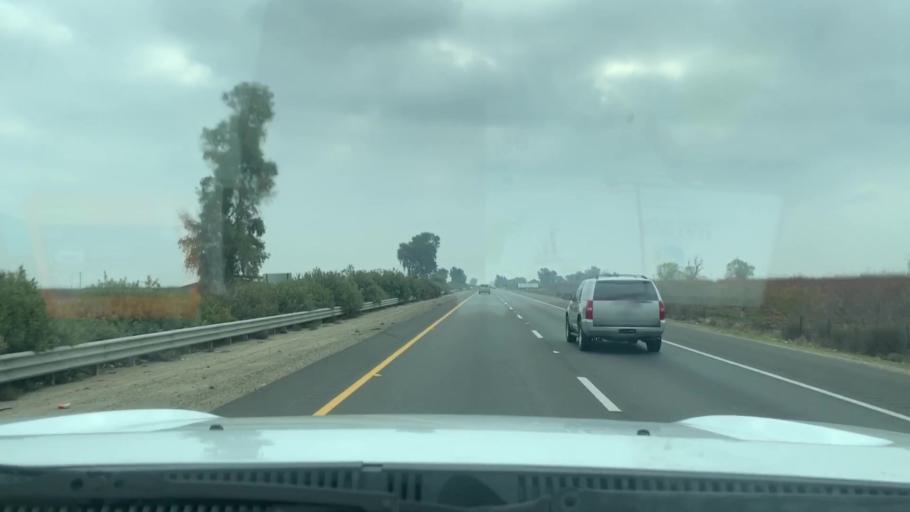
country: US
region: California
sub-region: Tulare County
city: Tipton
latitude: 36.1159
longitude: -119.3242
